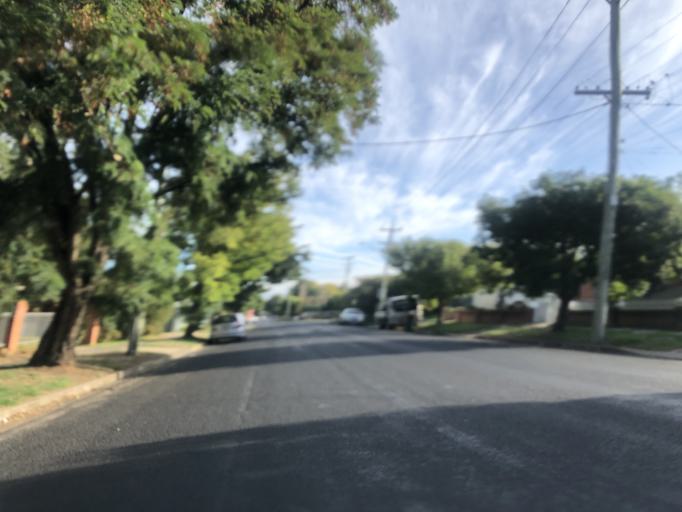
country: AU
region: New South Wales
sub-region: Orange Municipality
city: Orange
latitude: -33.2913
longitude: 149.0972
